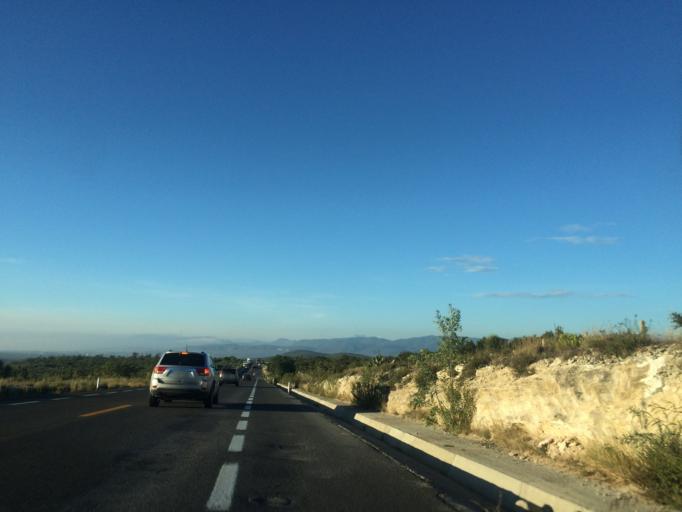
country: MX
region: Puebla
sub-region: Tehuacan
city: Magdalena Cuayucatepec
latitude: 18.6087
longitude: -97.4754
